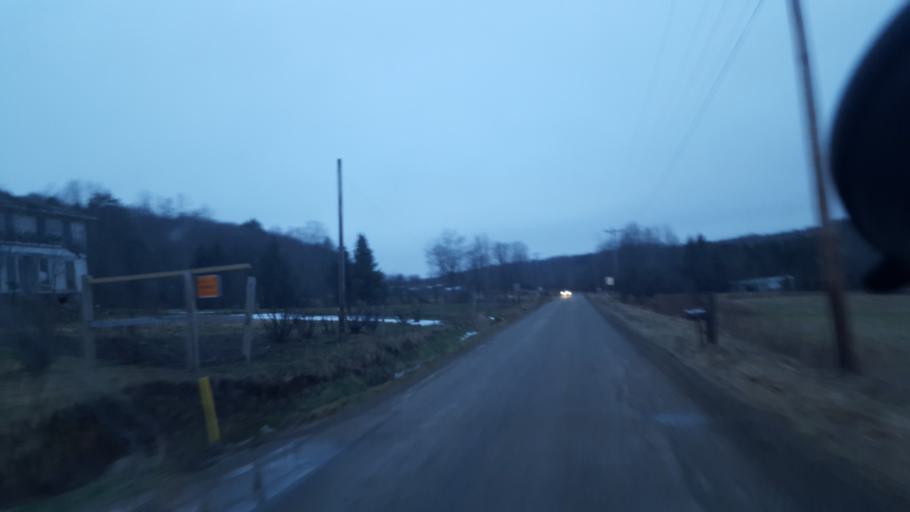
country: US
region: Pennsylvania
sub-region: Tioga County
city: Westfield
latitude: 41.9697
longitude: -77.7208
